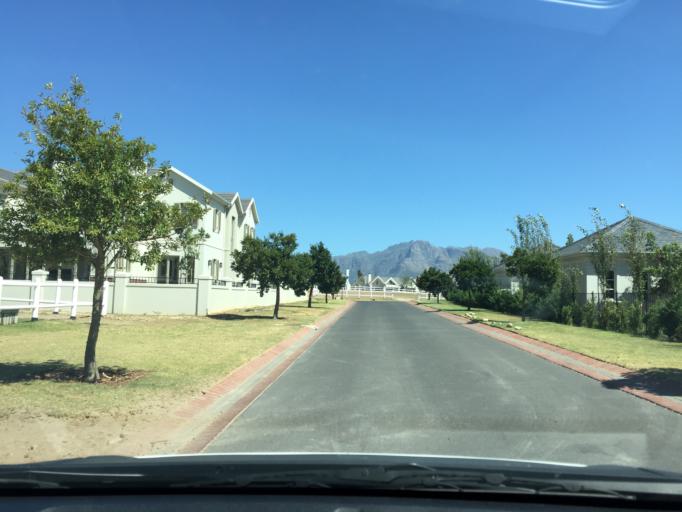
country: ZA
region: Western Cape
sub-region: Cape Winelands District Municipality
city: Paarl
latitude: -33.8054
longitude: 18.9767
